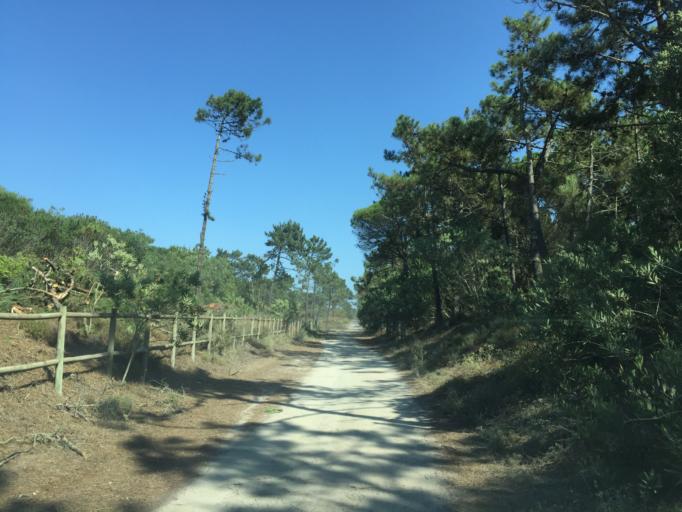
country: PT
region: Coimbra
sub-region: Figueira da Foz
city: Tavarede
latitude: 40.2638
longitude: -8.8649
